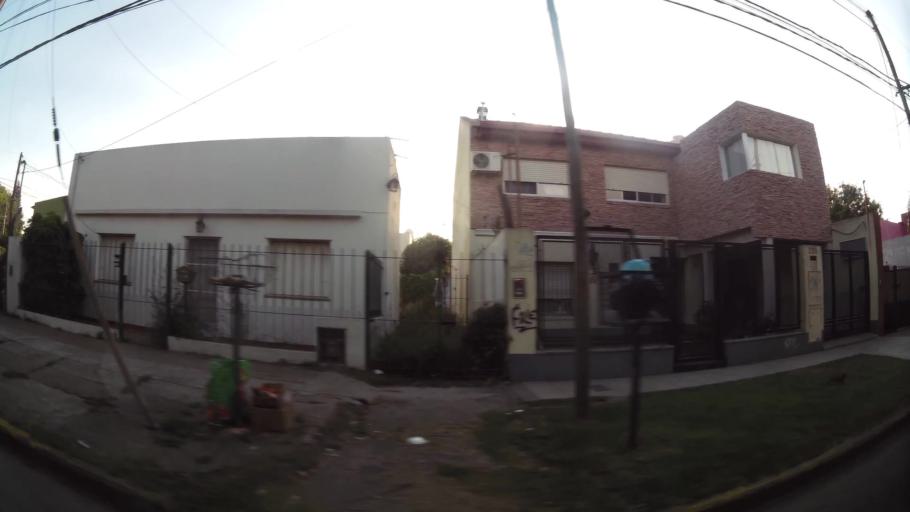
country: AR
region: Buenos Aires
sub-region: Partido de Tigre
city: Tigre
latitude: -34.4555
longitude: -58.6347
